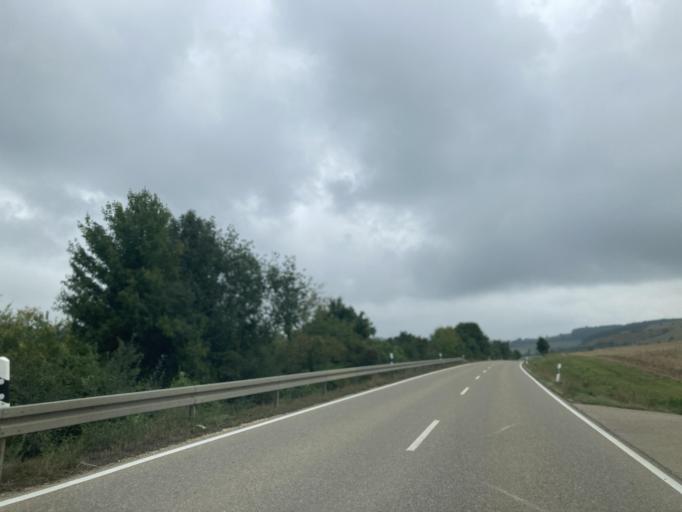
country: DE
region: Baden-Wuerttemberg
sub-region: Regierungsbezirk Stuttgart
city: Dischingen
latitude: 48.7045
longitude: 10.3705
